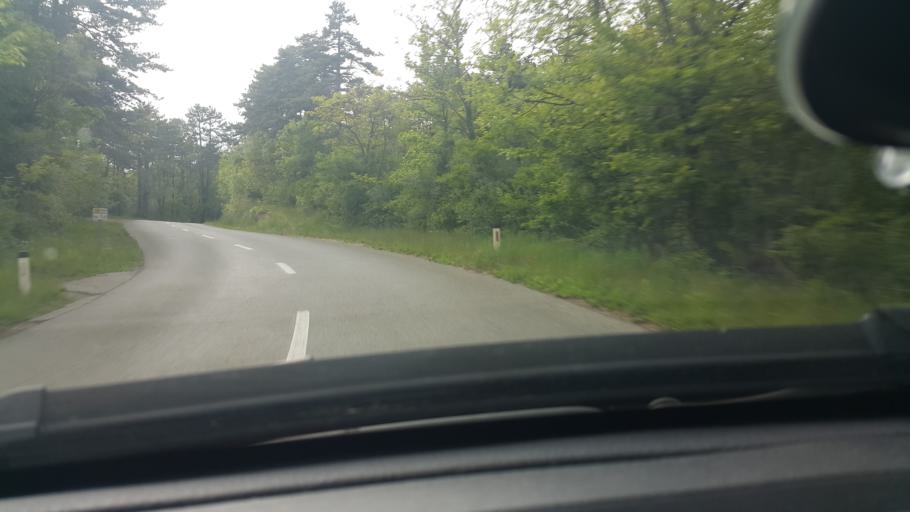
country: IT
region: Friuli Venezia Giulia
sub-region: Provincia di Trieste
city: Zolla
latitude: 45.7620
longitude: 13.8166
